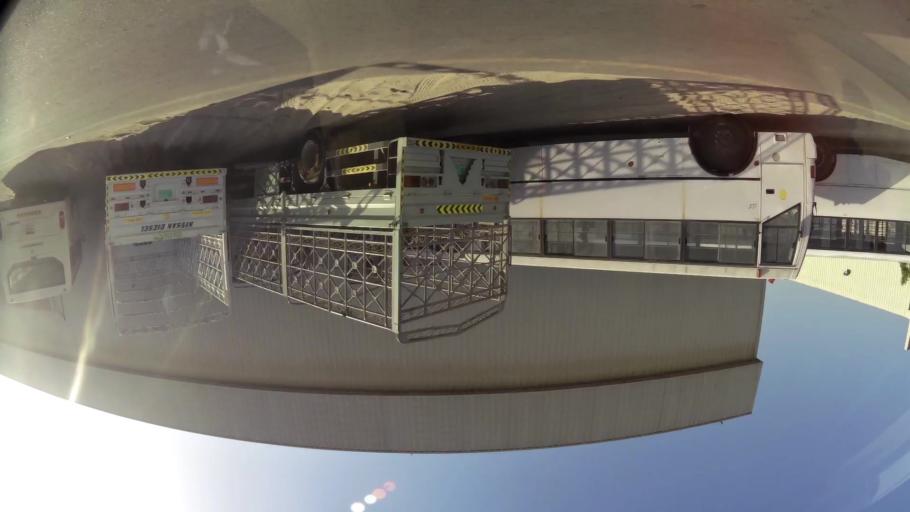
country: AE
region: Ash Shariqah
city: Sharjah
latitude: 25.2849
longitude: 55.3856
